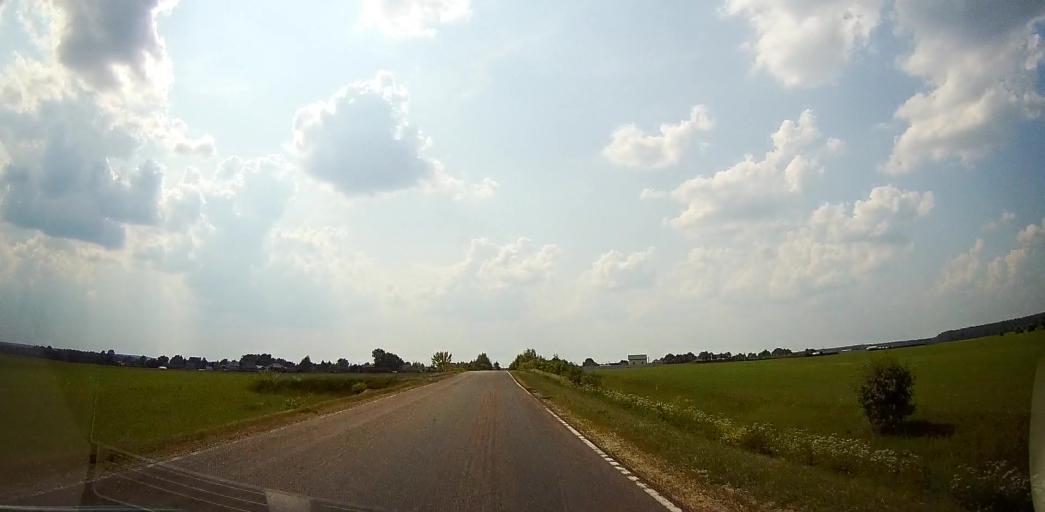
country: RU
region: Moskovskaya
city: Malino
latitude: 55.0642
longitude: 38.1135
